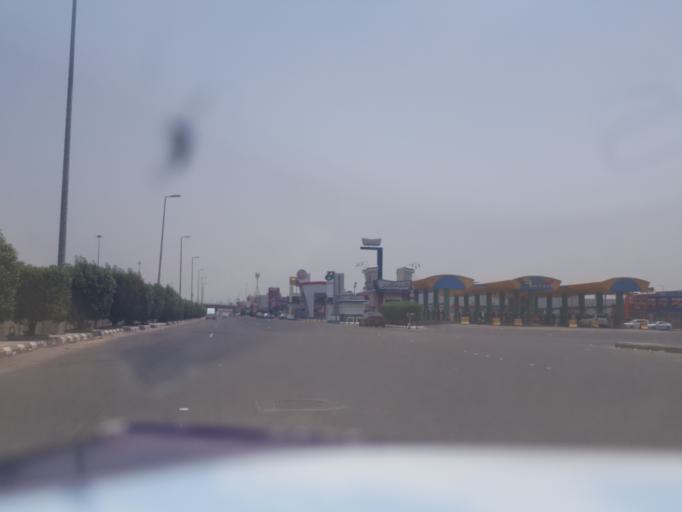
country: SA
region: Makkah
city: Jeddah
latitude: 21.4426
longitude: 39.2772
